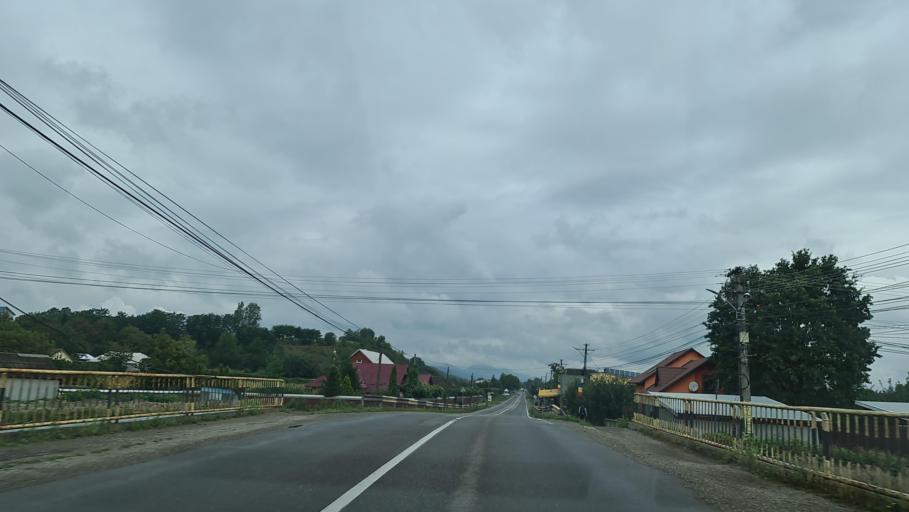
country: RO
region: Neamt
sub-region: Comuna Borlesti
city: Ruseni
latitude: 46.8036
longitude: 26.5288
